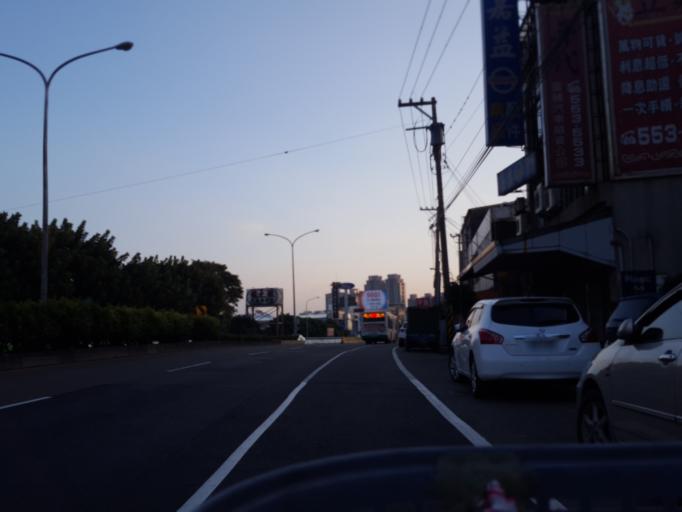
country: TW
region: Taiwan
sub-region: Hsinchu
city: Zhubei
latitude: 24.8362
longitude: 121.0050
